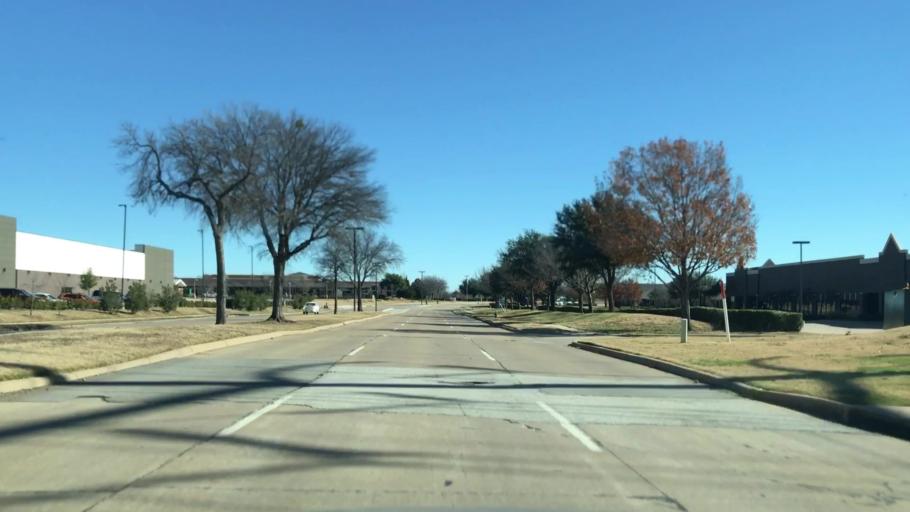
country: US
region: Texas
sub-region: Dallas County
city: Coppell
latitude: 32.9193
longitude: -96.9848
